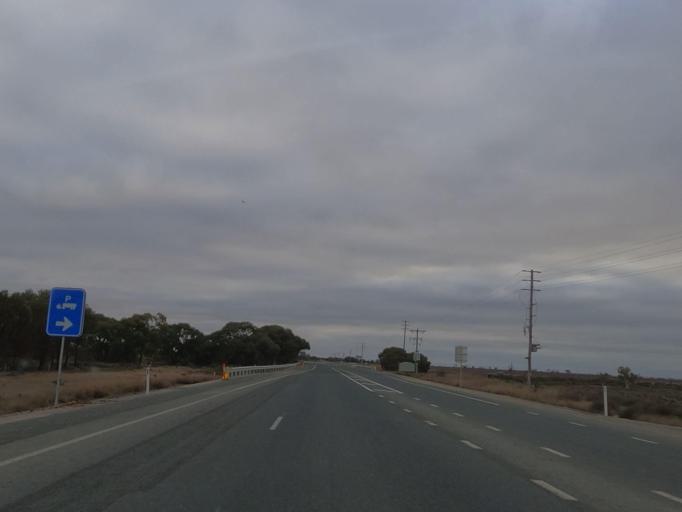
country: AU
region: Victoria
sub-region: Swan Hill
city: Swan Hill
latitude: -35.5456
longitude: 143.7601
